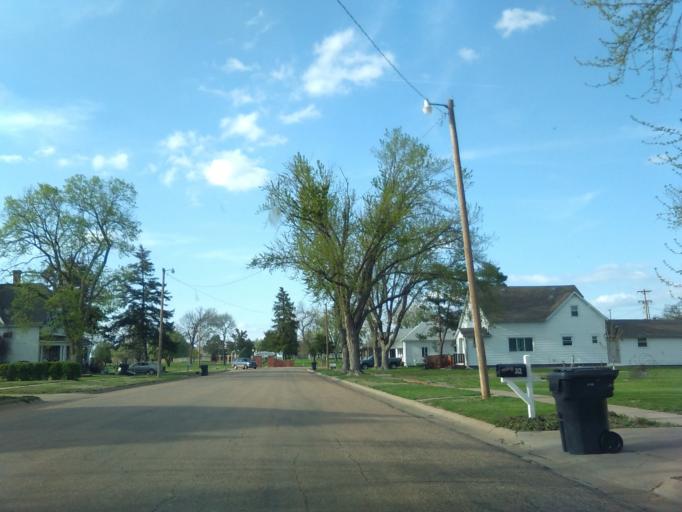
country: US
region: Nebraska
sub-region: Franklin County
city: Franklin
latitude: 40.0987
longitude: -98.9536
